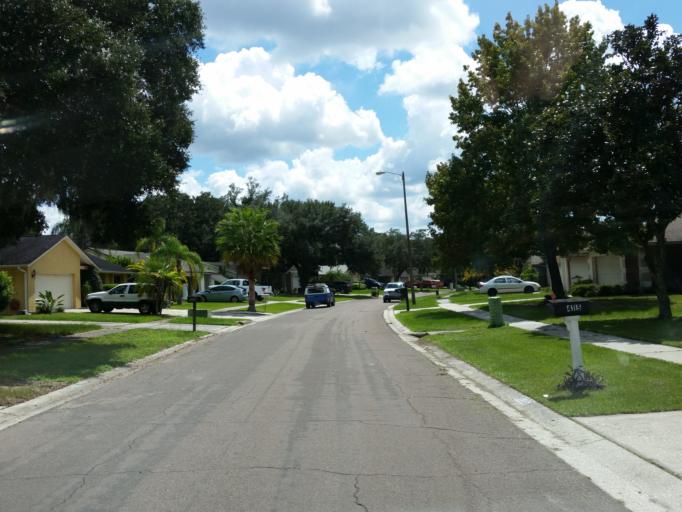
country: US
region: Florida
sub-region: Hillsborough County
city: Bloomingdale
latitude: 27.8777
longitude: -82.2714
